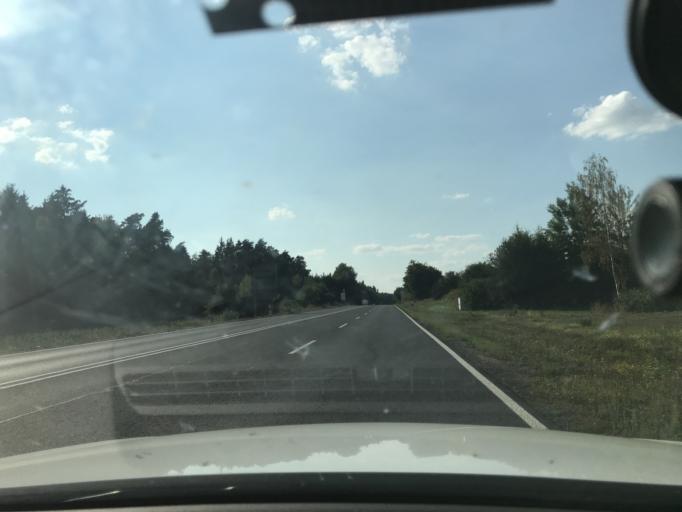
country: DE
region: Bavaria
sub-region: Upper Palatinate
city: Poppenricht
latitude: 49.4656
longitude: 11.7797
